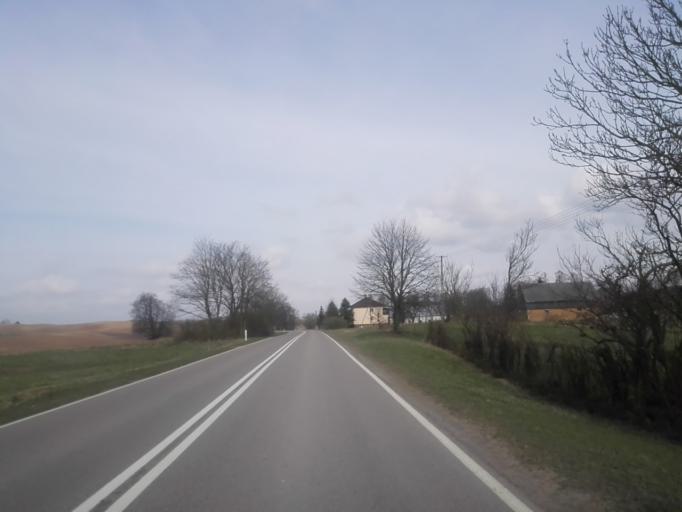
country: PL
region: Podlasie
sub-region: Powiat sejnenski
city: Sejny
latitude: 54.0830
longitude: 23.3476
